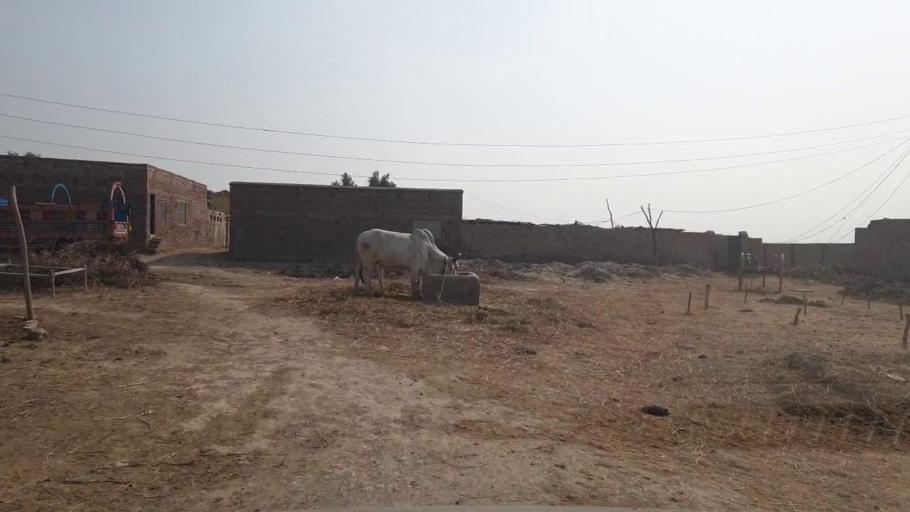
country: PK
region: Sindh
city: Tando Muhammad Khan
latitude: 25.0481
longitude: 68.3944
